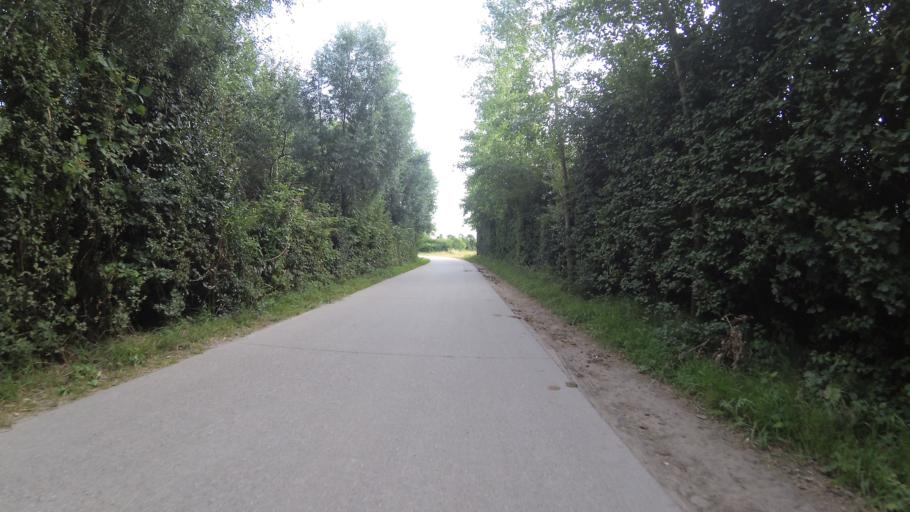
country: NL
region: Zeeland
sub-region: Gemeente Middelburg
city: Middelburg
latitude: 51.5598
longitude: 3.5212
